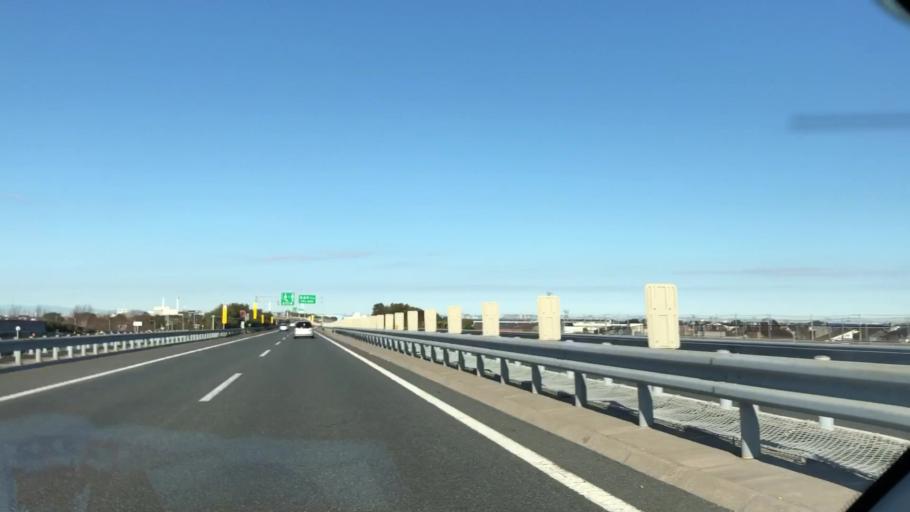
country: JP
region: Chiba
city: Kisarazu
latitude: 35.4286
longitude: 139.9279
